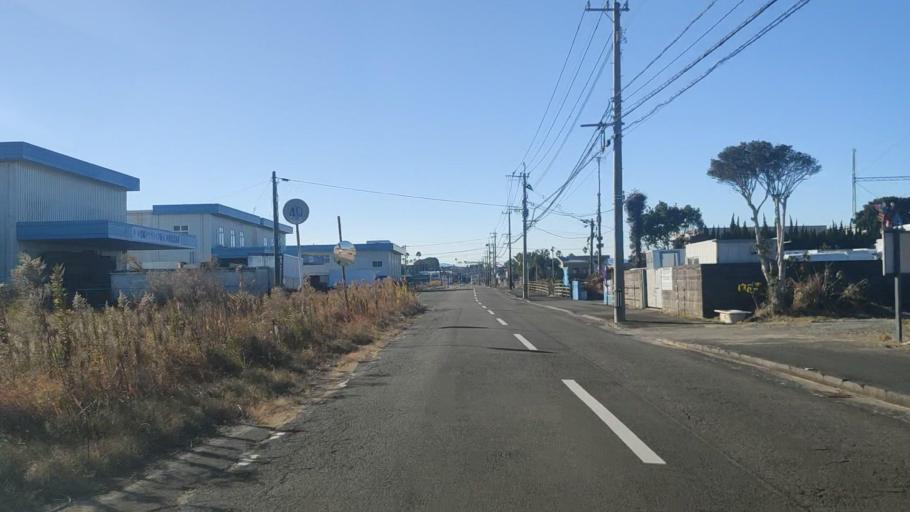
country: JP
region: Miyazaki
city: Miyazaki-shi
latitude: 31.8679
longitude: 131.4409
